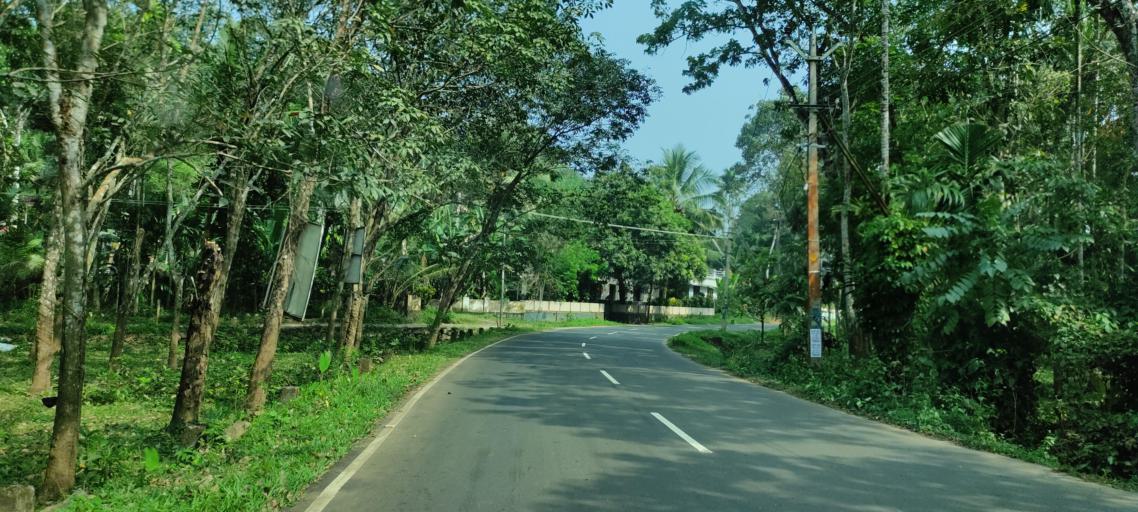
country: IN
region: Kerala
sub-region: Pattanamtitta
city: Adur
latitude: 9.2311
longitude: 76.6983
